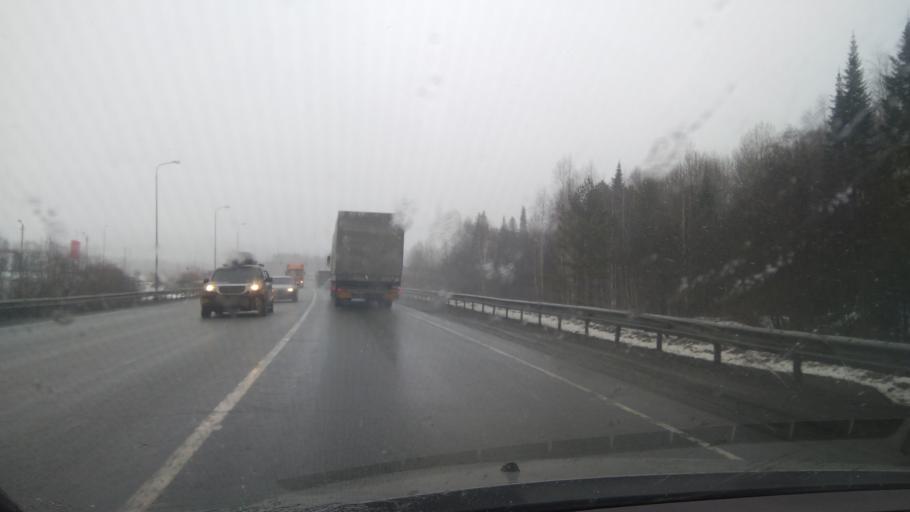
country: RU
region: Sverdlovsk
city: Arti
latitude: 56.7909
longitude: 58.6014
